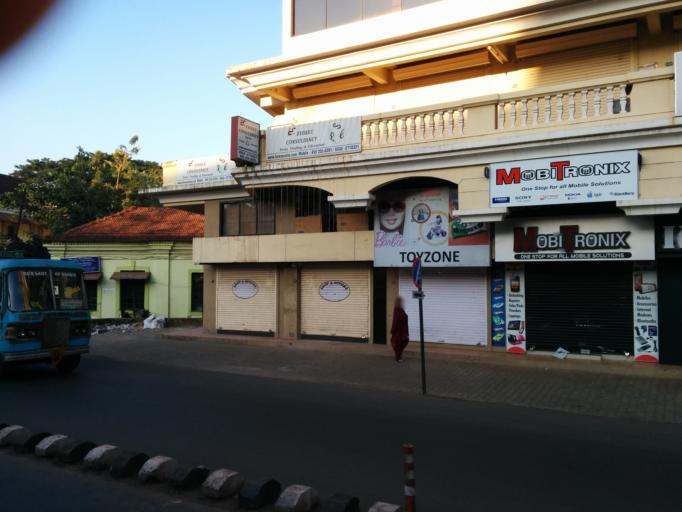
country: IN
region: Goa
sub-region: South Goa
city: Madgaon
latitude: 15.2797
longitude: 73.9601
